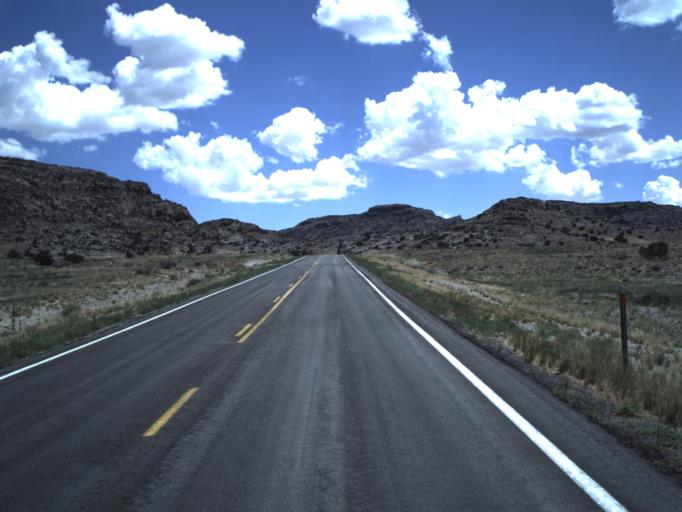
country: US
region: Utah
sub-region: Beaver County
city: Milford
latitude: 39.0730
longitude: -113.6657
